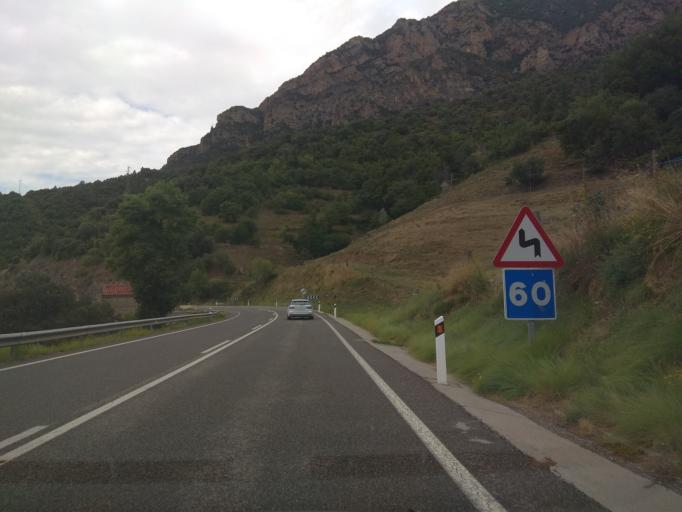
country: ES
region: Catalonia
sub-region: Provincia de Lleida
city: el Pont de Bar
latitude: 42.3620
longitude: 1.5748
